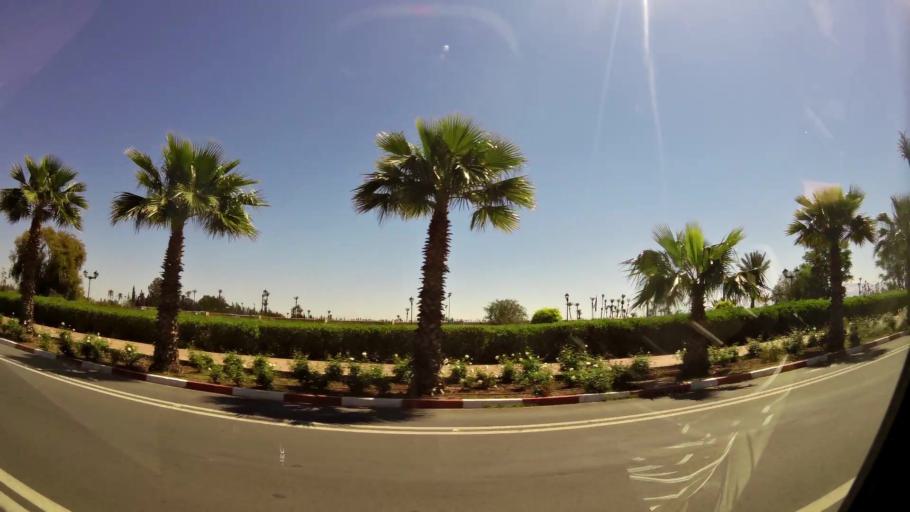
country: MA
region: Marrakech-Tensift-Al Haouz
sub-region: Marrakech
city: Marrakesh
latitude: 31.5988
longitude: -7.9872
